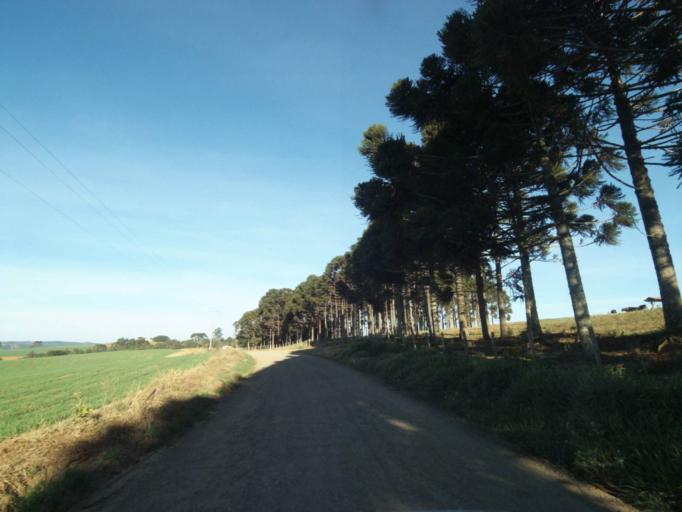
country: BR
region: Parana
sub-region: Telemaco Borba
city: Telemaco Borba
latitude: -24.5198
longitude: -50.6457
